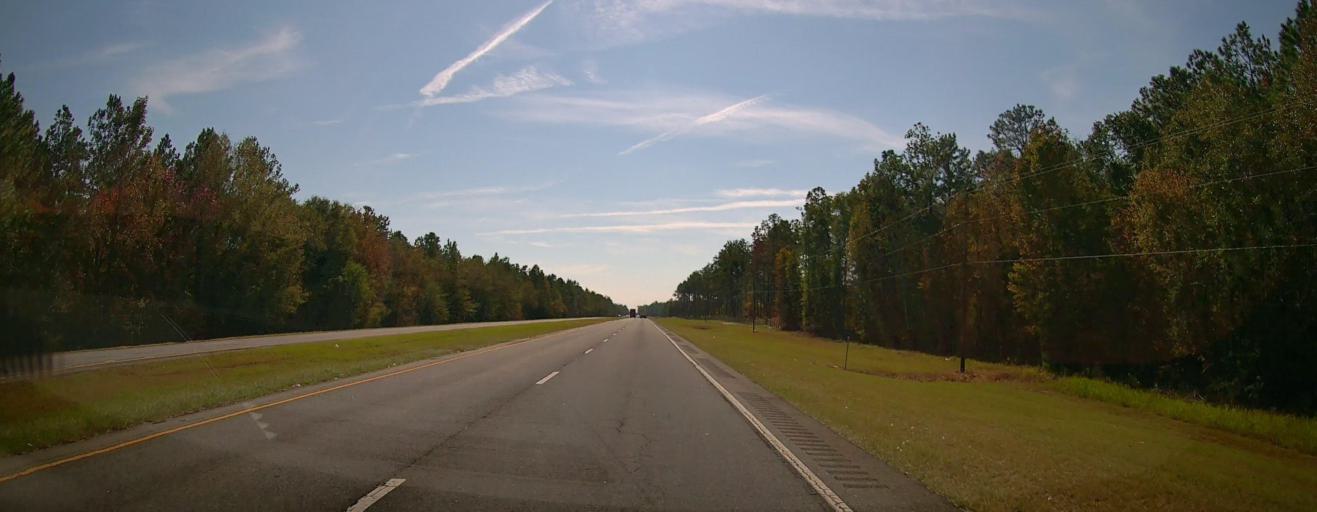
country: US
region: Georgia
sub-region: Lee County
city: Leesburg
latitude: 31.7959
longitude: -83.9588
